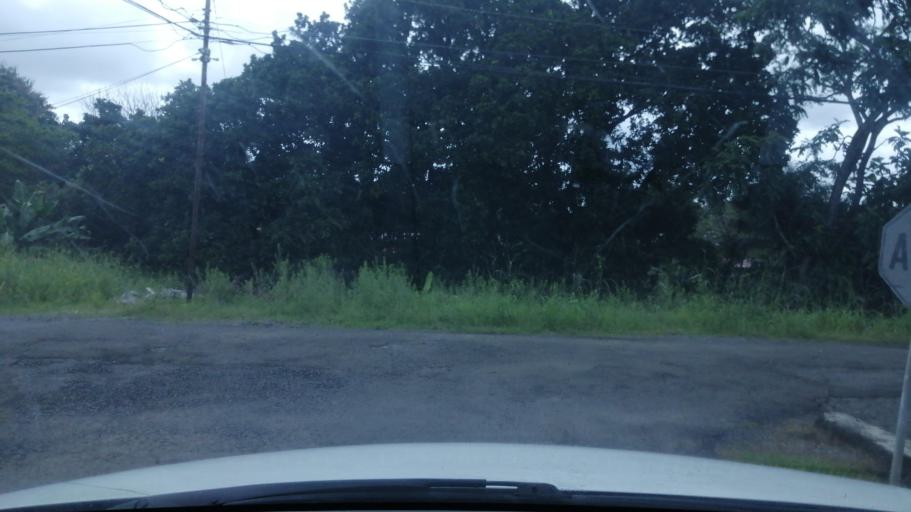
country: PA
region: Chiriqui
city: David
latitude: 8.4421
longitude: -82.4197
